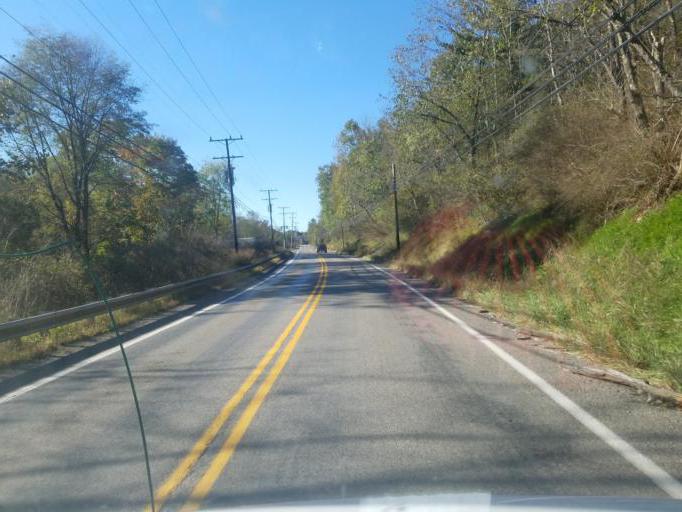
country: US
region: Pennsylvania
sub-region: Allegheny County
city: Imperial
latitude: 40.4595
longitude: -80.2604
